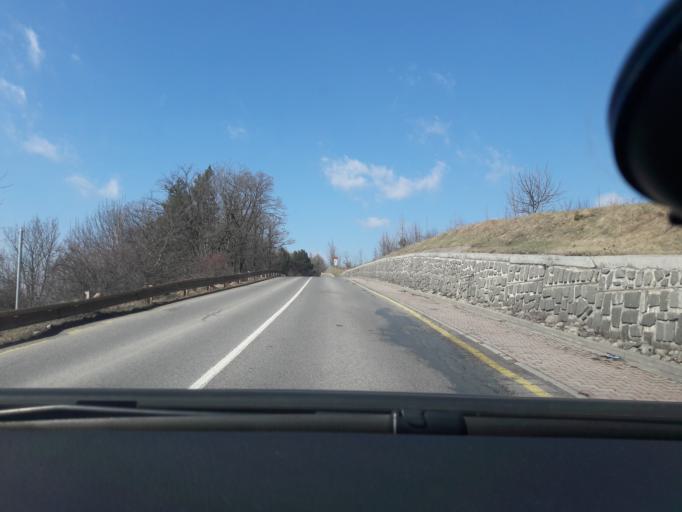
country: SK
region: Zilinsky
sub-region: Okres Liptovsky Mikulas
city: Liptovsky Mikulas
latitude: 49.0968
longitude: 19.5851
